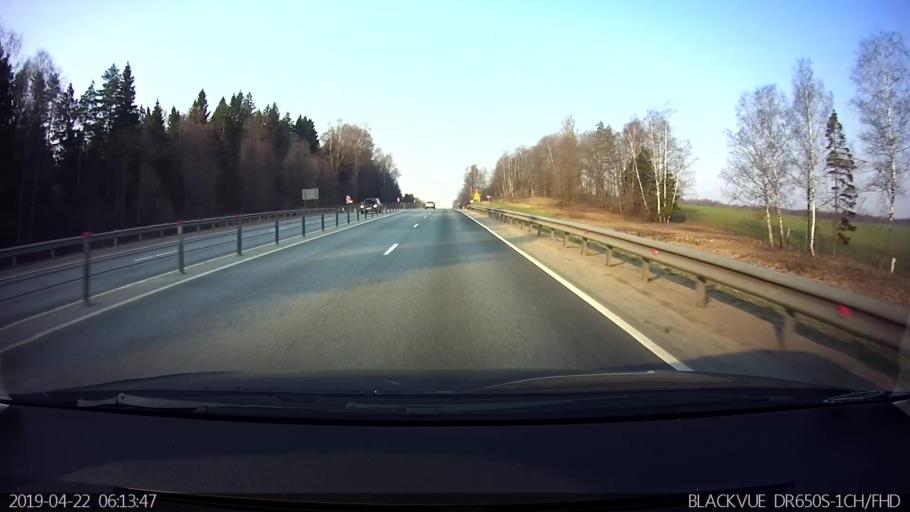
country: RU
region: Moskovskaya
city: Mozhaysk
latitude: 55.4685
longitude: 36.0947
